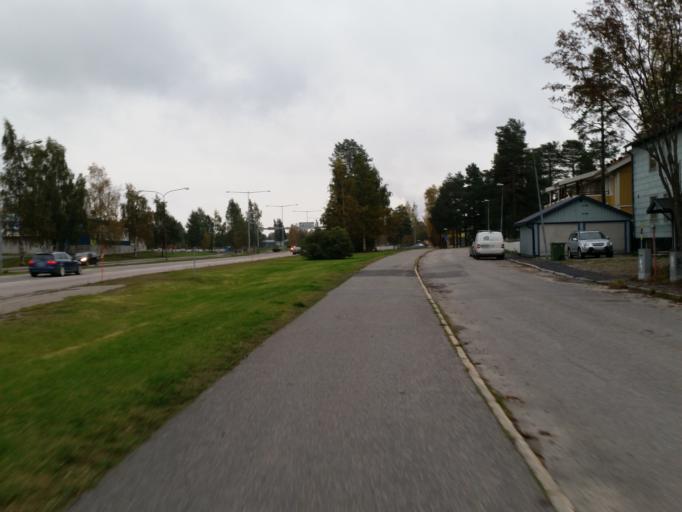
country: SE
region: Norrbotten
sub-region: Lulea Kommun
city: Lulea
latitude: 65.5793
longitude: 22.1948
